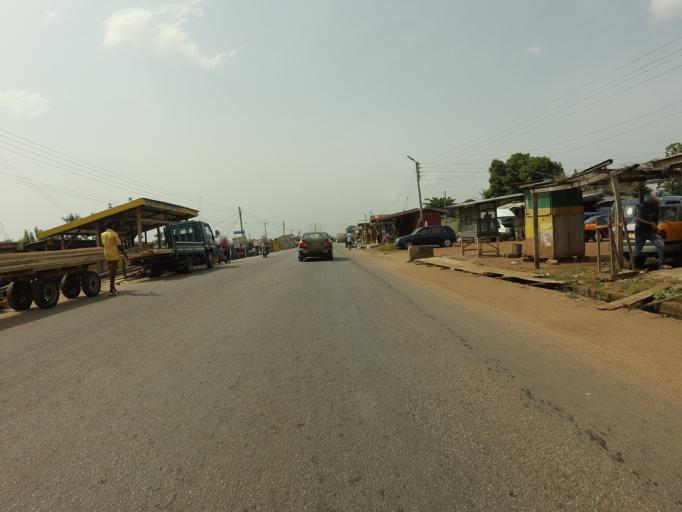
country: GH
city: Akropong
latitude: 6.2505
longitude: 0.1310
